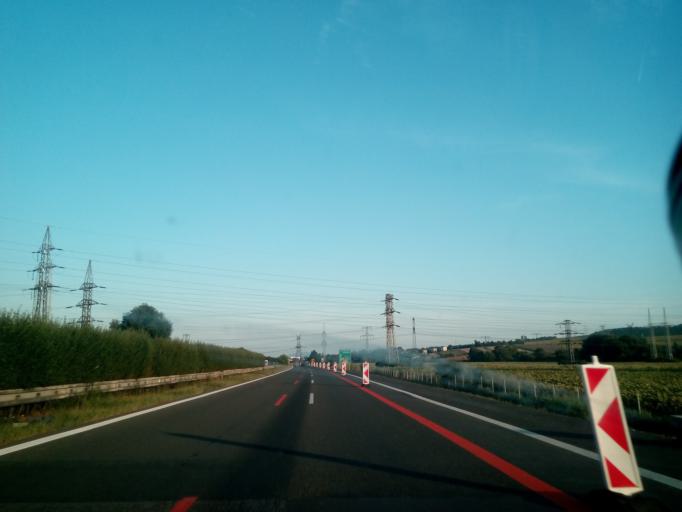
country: SK
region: Presovsky
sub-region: Okres Presov
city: Presov
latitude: 48.8657
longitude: 21.2588
